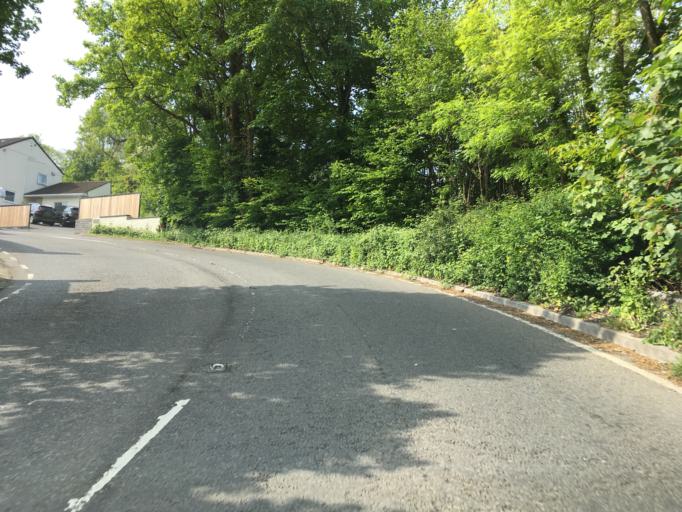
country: GB
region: England
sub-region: North Somerset
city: Dundry
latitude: 51.4024
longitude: -2.6235
